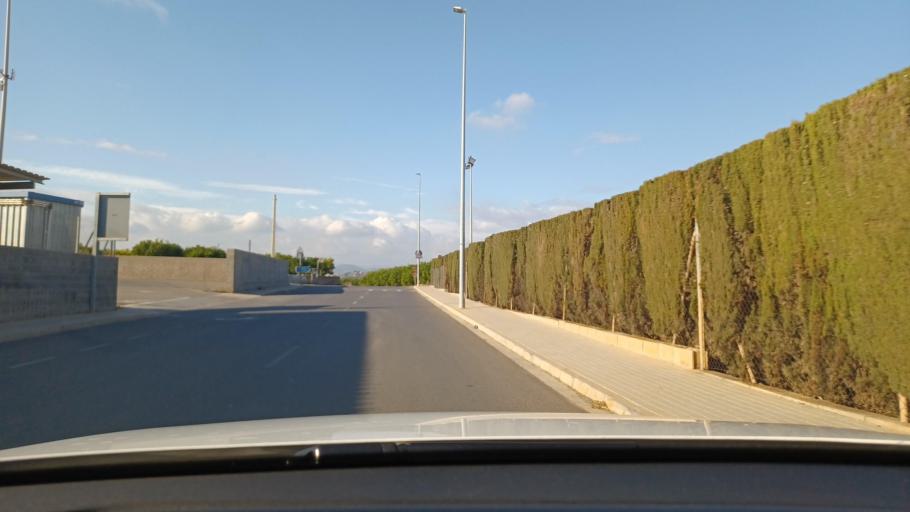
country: ES
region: Valencia
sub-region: Provincia de Castello
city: Betxi
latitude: 39.9338
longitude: -0.2039
